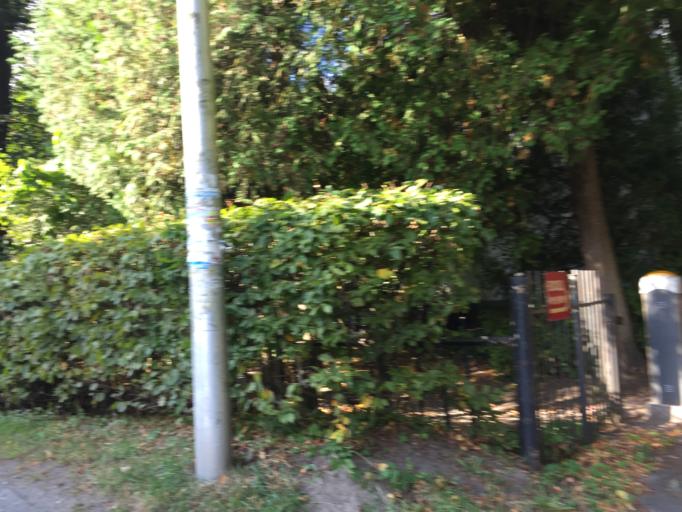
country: RU
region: Kaliningrad
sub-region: Gorod Svetlogorsk
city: Svetlogorsk
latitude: 54.9417
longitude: 20.1499
